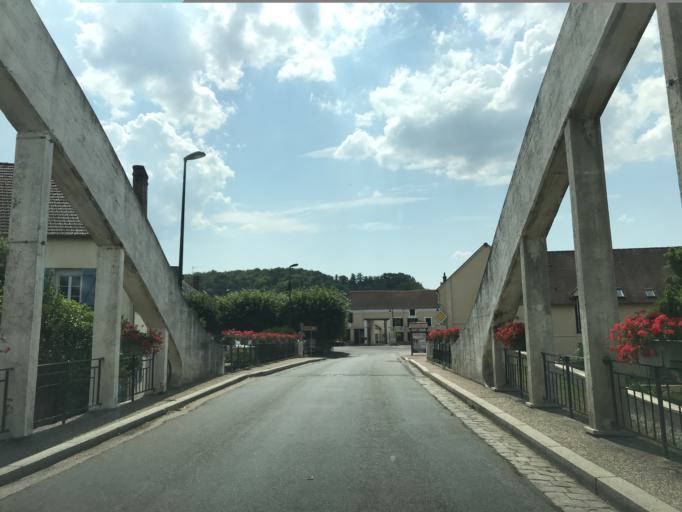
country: FR
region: Haute-Normandie
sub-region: Departement de l'Eure
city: Garennes-sur-Eure
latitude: 48.9102
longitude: 1.4417
